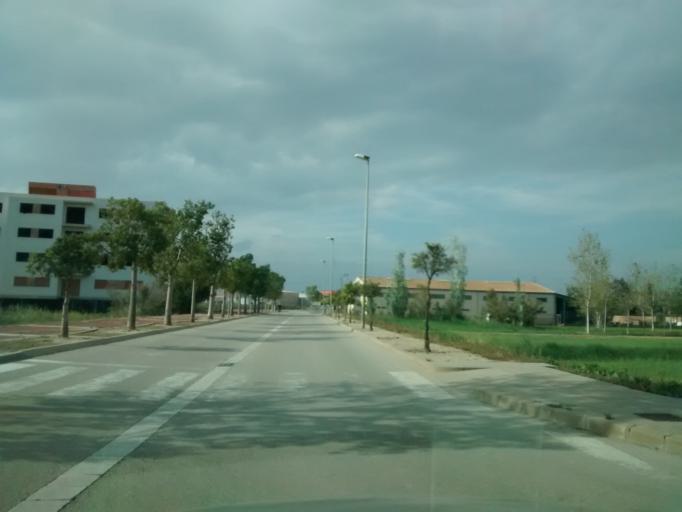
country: ES
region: Catalonia
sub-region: Provincia de Tarragona
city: Deltebre
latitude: 40.7224
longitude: 0.7210
